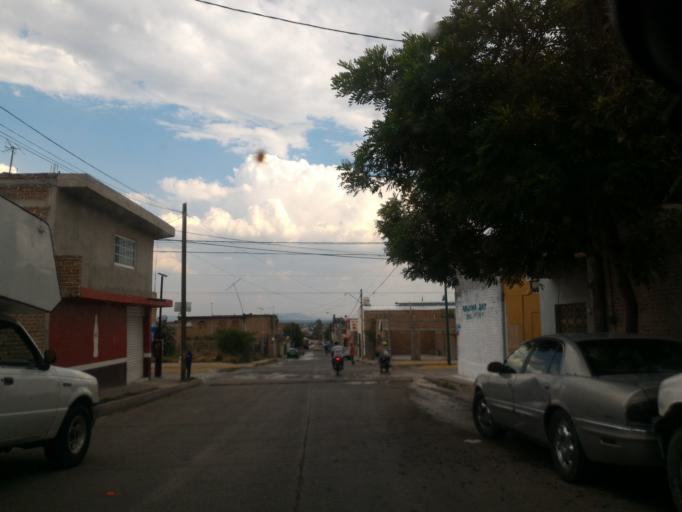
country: MX
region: Guanajuato
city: San Francisco del Rincon
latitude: 21.0431
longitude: -101.8567
